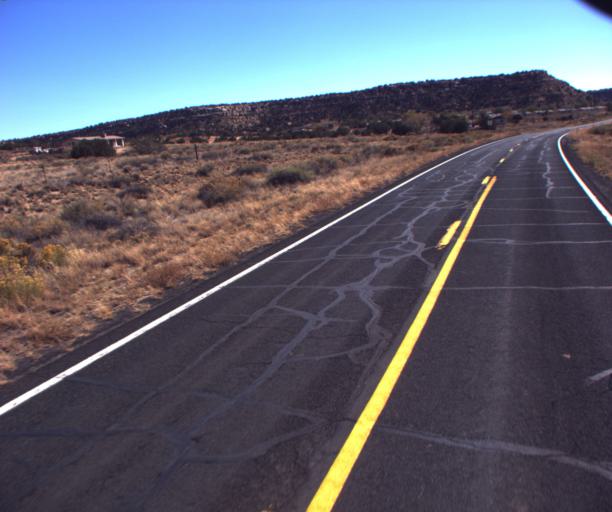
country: US
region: Arizona
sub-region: Navajo County
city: First Mesa
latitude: 35.8281
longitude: -110.2226
